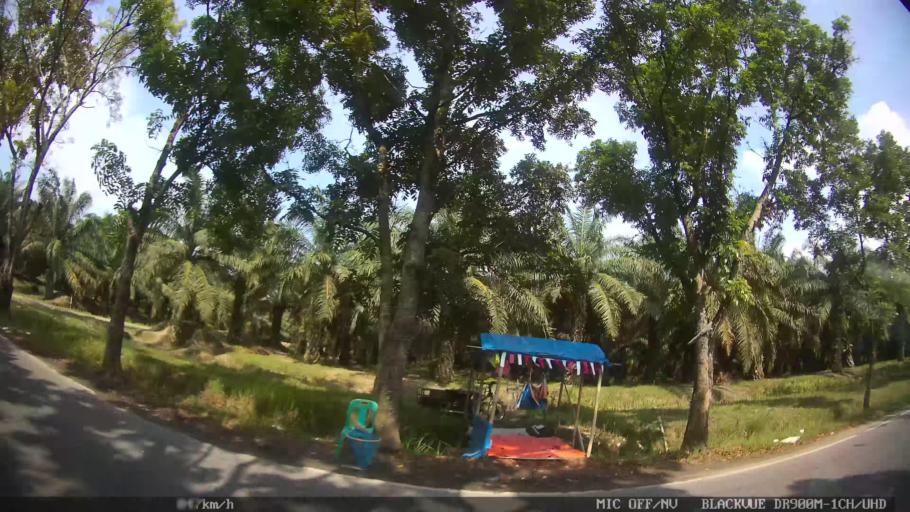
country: ID
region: North Sumatra
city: Binjai
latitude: 3.6444
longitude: 98.5355
